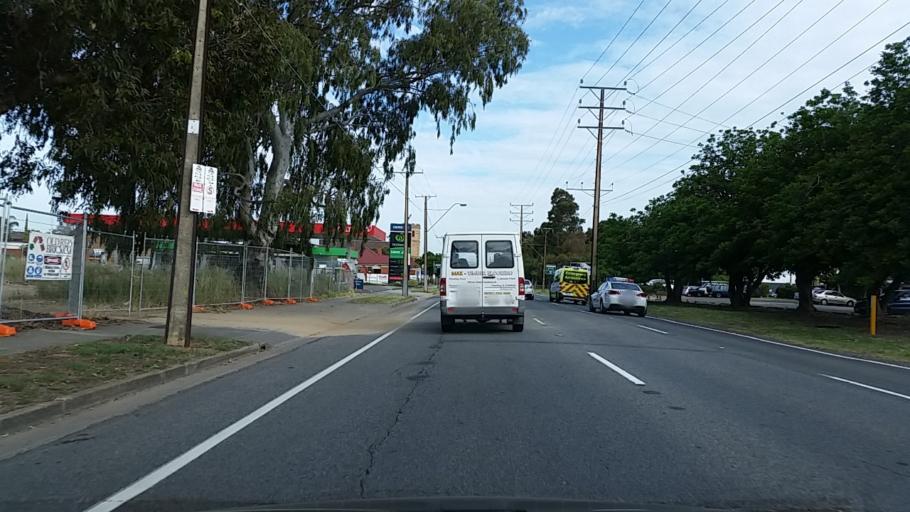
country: AU
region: South Australia
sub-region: Charles Sturt
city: Woodville West
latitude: -34.8792
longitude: 138.5333
